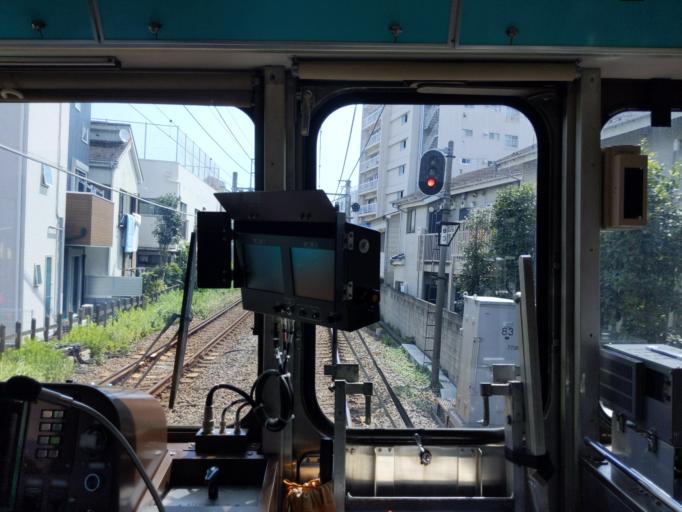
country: JP
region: Kanagawa
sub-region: Kawasaki-shi
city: Kawasaki
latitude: 35.5721
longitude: 139.6935
